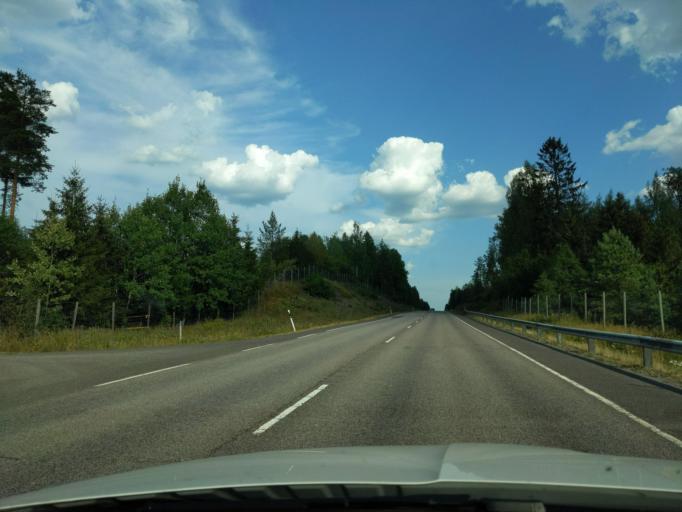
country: FI
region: Paijanne Tavastia
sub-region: Lahti
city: Hollola
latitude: 60.9981
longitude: 25.3474
